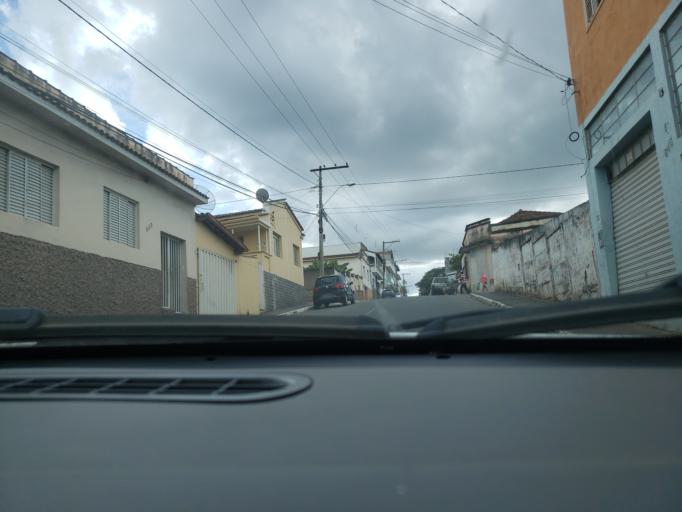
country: BR
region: Minas Gerais
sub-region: Campo Belo
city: Campo Belo
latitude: -20.8998
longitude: -45.2687
